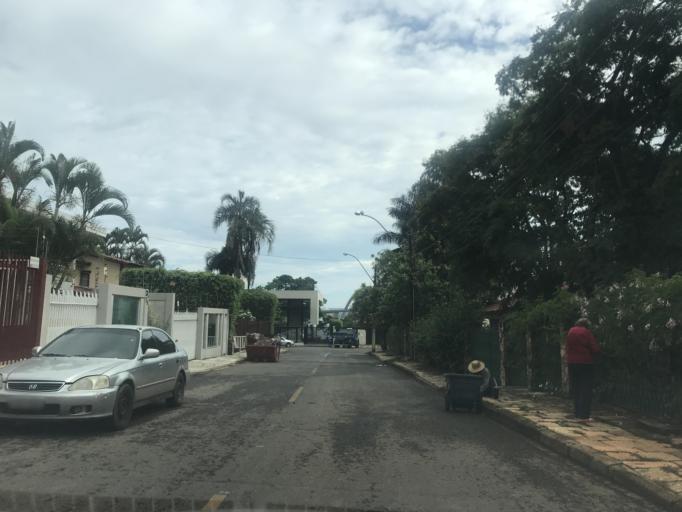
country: BR
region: Federal District
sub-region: Brasilia
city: Brasilia
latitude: -15.8329
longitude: -47.8308
